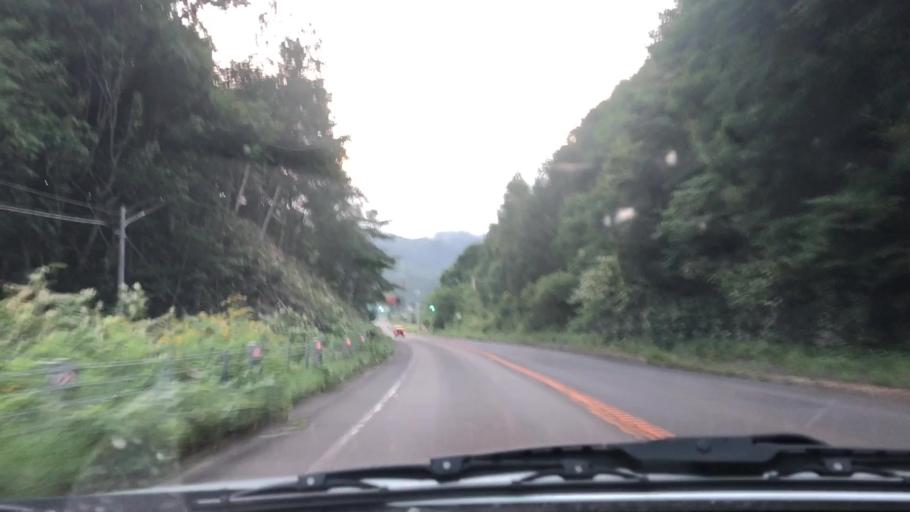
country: JP
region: Hokkaido
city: Iwamizawa
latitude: 42.9372
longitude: 142.0492
